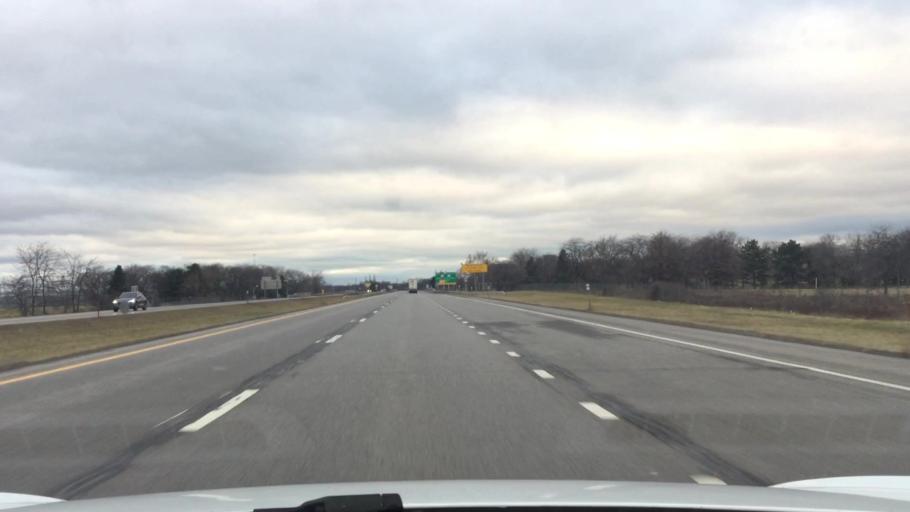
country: US
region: New York
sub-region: Niagara County
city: Lewiston
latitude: 43.1332
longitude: -79.0196
